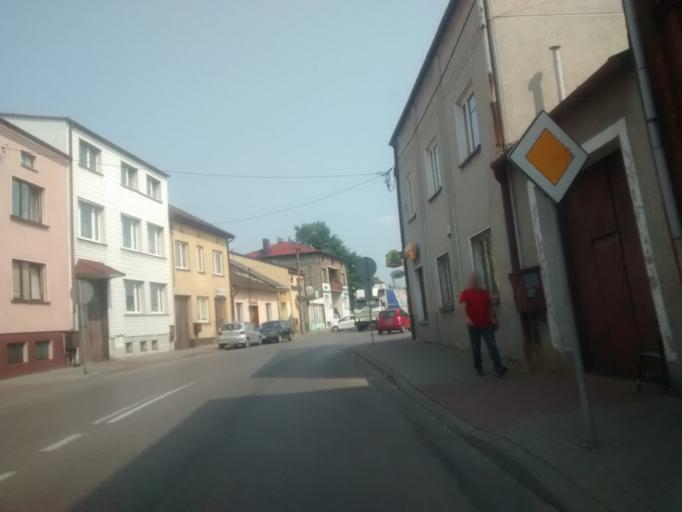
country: PL
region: Silesian Voivodeship
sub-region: Powiat myszkowski
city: Zarki
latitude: 50.6256
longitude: 19.3634
